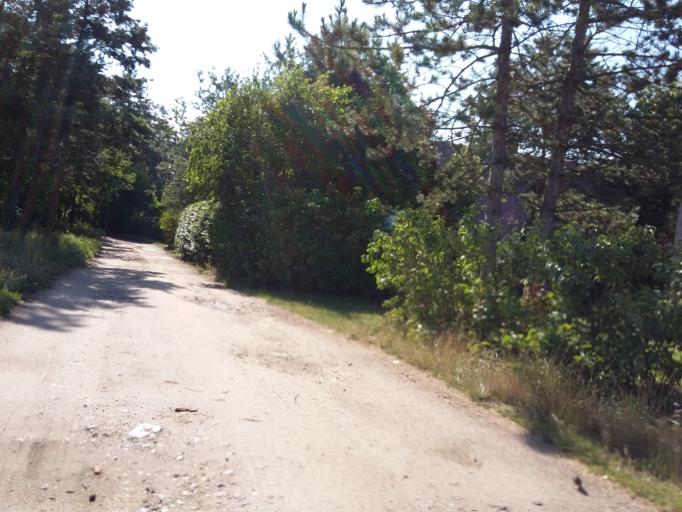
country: AT
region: Lower Austria
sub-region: Politischer Bezirk Ganserndorf
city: Drosing
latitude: 48.4979
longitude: 16.9562
